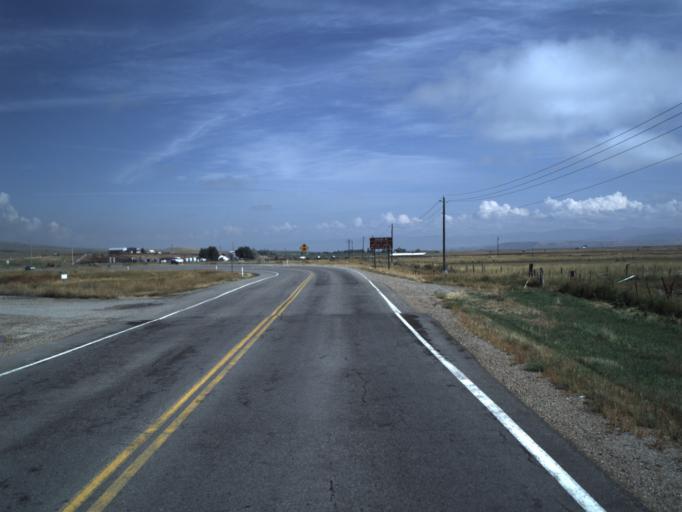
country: US
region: Utah
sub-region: Rich County
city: Randolph
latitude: 41.7694
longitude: -111.1231
